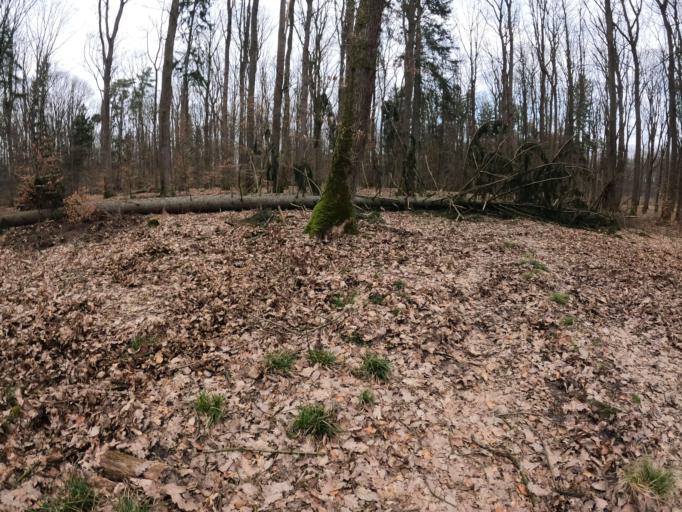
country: PL
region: West Pomeranian Voivodeship
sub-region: Powiat kamienski
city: Golczewo
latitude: 53.8112
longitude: 15.0211
